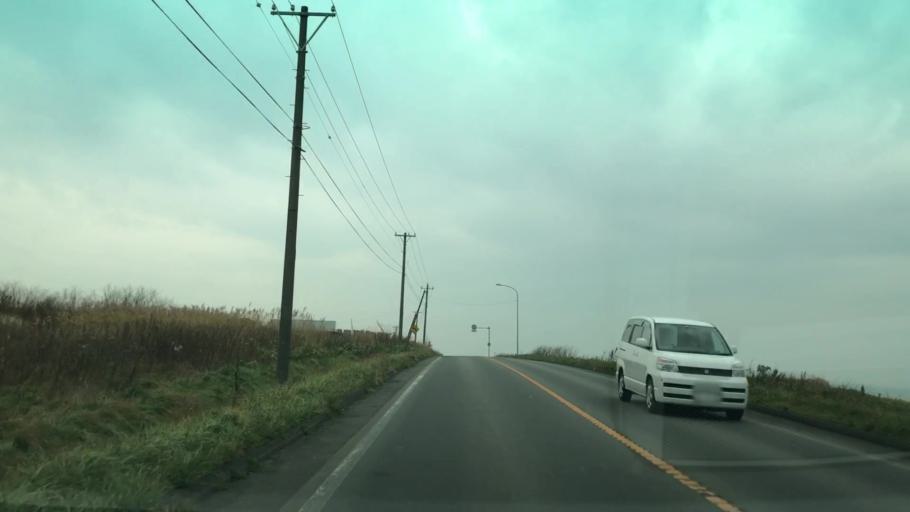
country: JP
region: Hokkaido
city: Ishikari
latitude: 43.3510
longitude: 141.4261
